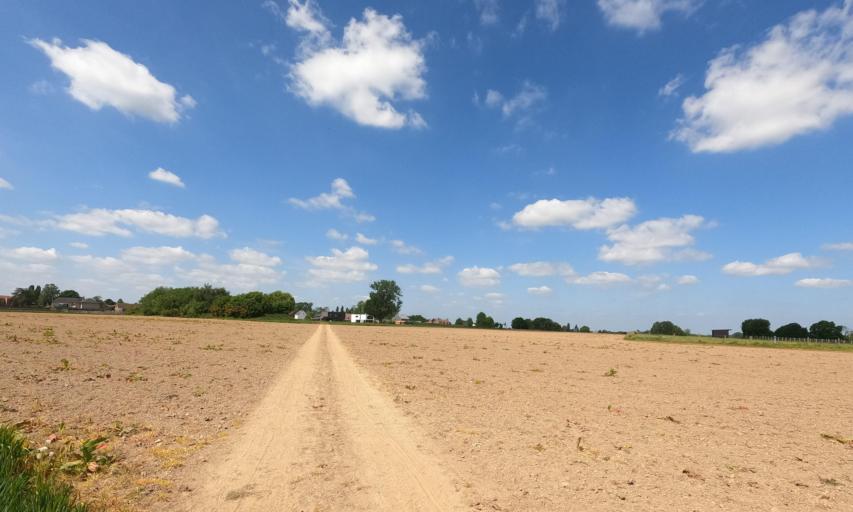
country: BE
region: Flanders
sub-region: Provincie Vlaams-Brabant
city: Opwijk
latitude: 50.9613
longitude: 4.1976
